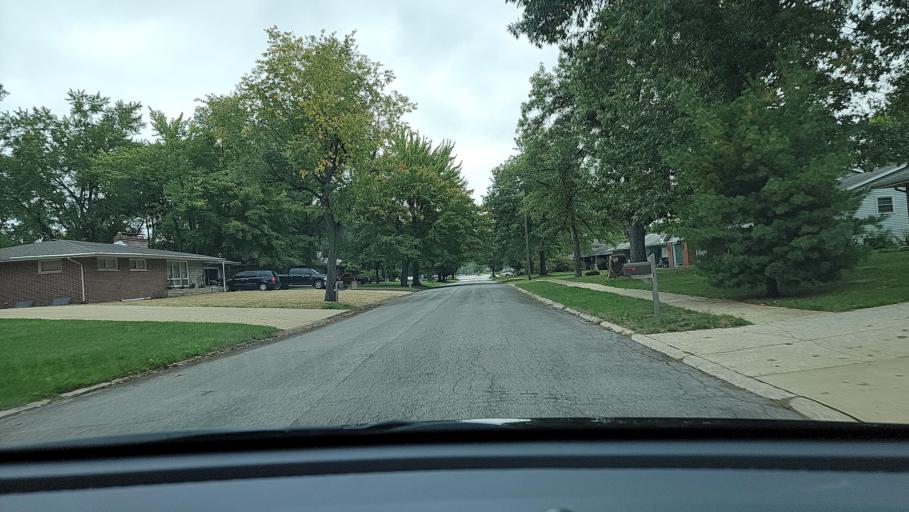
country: US
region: Indiana
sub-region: Porter County
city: Portage
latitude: 41.5736
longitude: -87.1763
